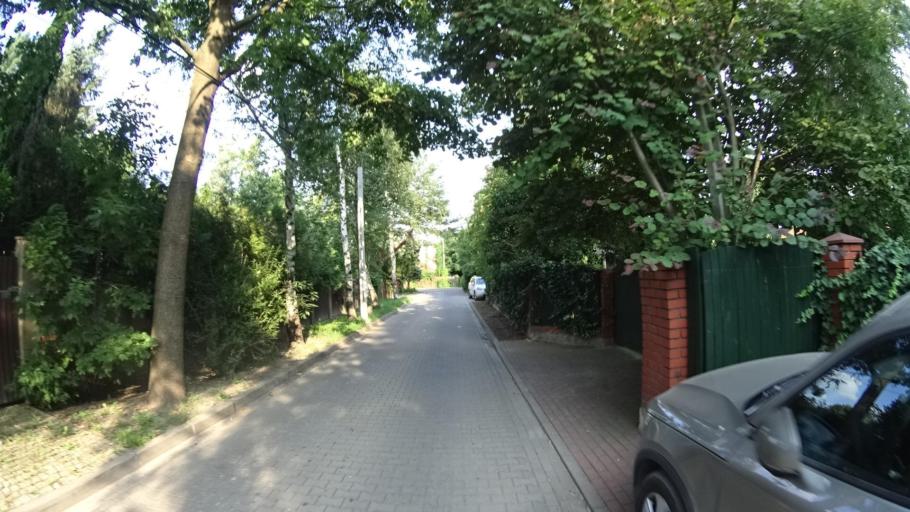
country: PL
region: Masovian Voivodeship
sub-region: Powiat pruszkowski
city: Michalowice
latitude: 52.1770
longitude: 20.8781
